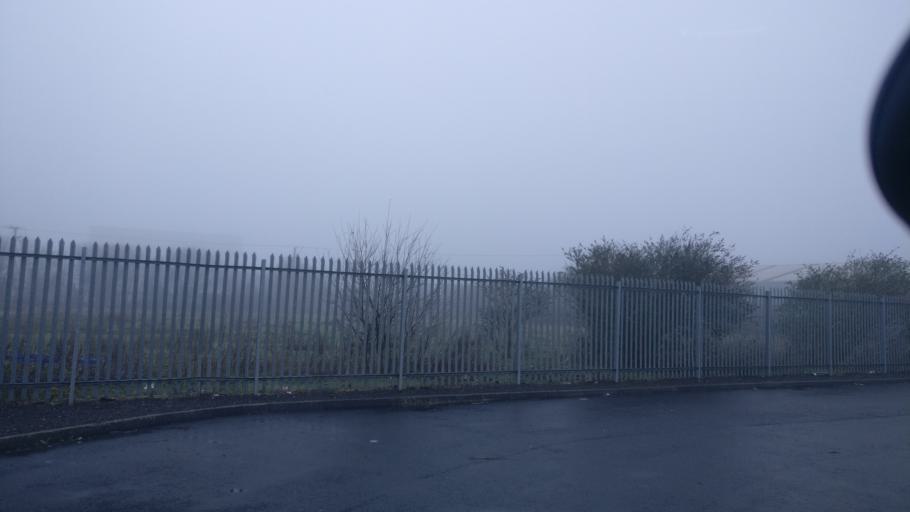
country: IE
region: Munster
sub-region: County Limerick
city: Luimneach
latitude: 52.6494
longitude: -8.5917
